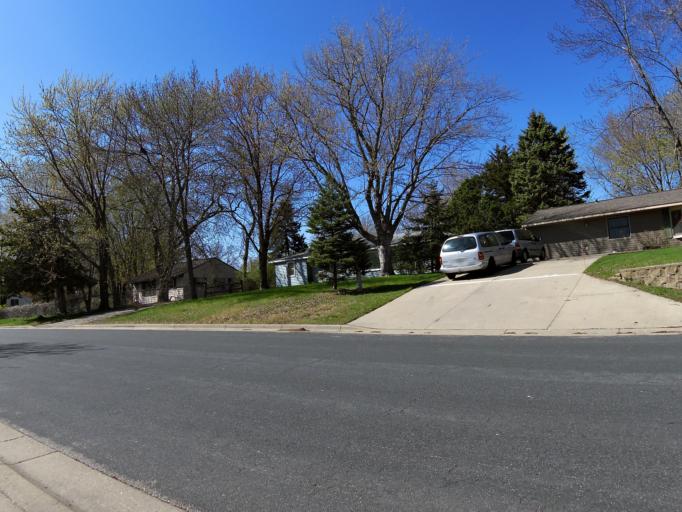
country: US
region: Minnesota
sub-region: Scott County
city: Prior Lake
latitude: 44.7127
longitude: -93.4319
